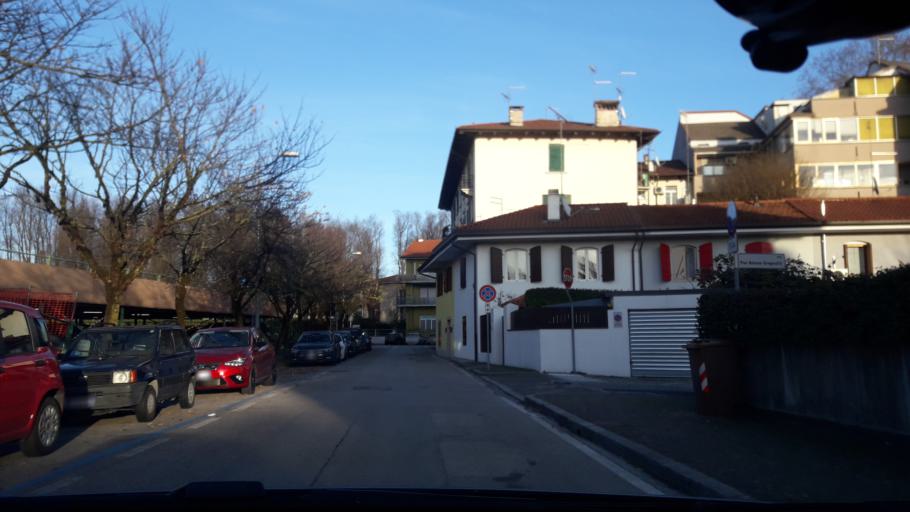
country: IT
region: Friuli Venezia Giulia
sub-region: Provincia di Udine
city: Udine
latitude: 46.0548
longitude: 13.2452
